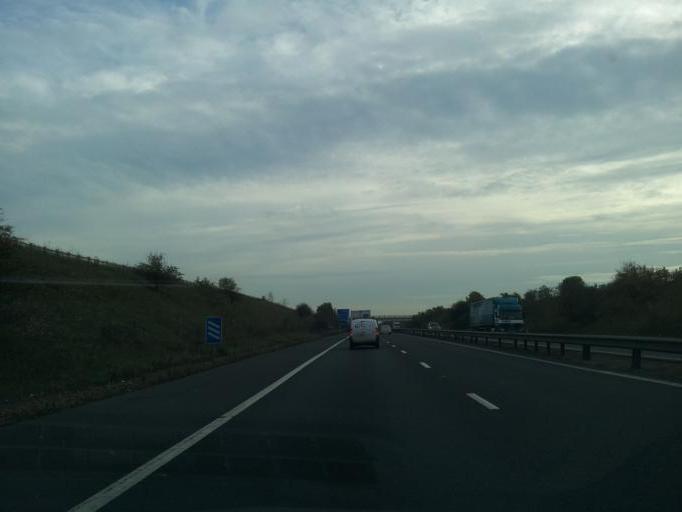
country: GB
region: England
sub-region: Cambridgeshire
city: Duxford
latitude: 52.1053
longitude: 0.1323
